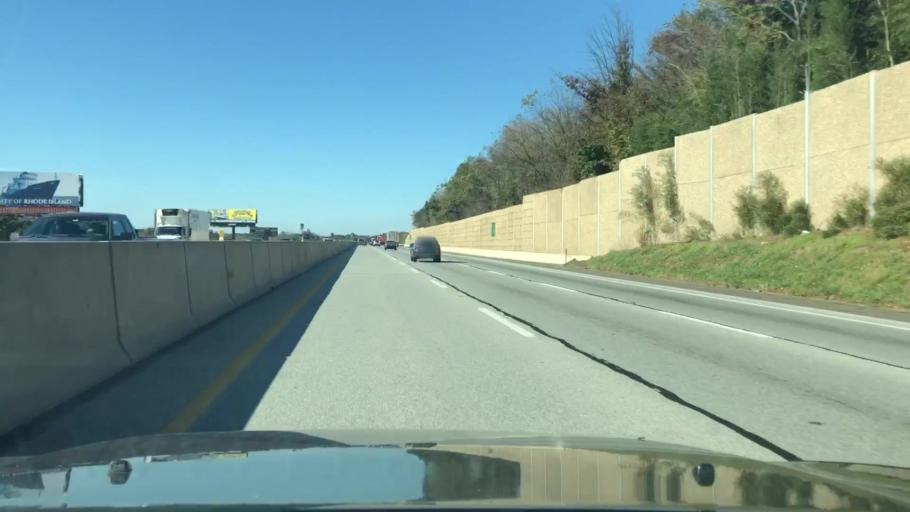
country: US
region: Pennsylvania
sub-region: Bucks County
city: Warminster Heights
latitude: 40.1636
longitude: -75.0596
